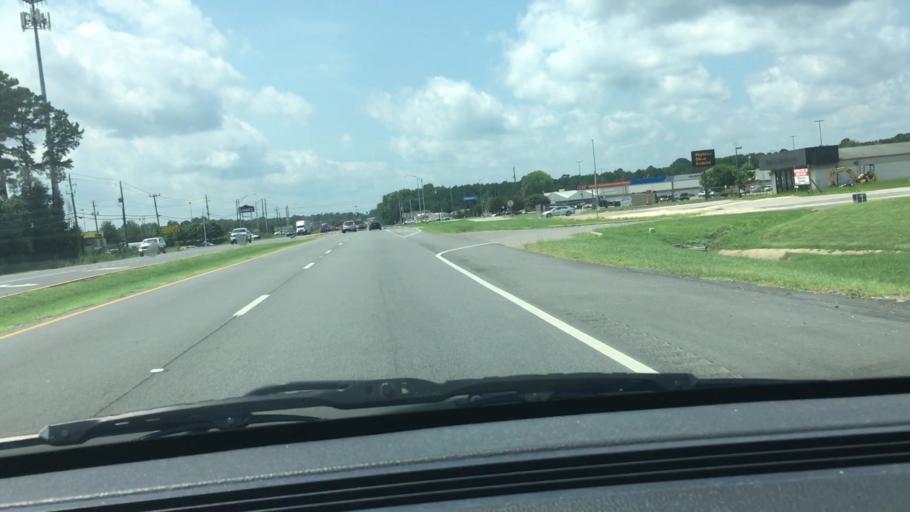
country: US
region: Alabama
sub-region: Tuscaloosa County
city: Northport
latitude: 33.2362
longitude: -87.6114
